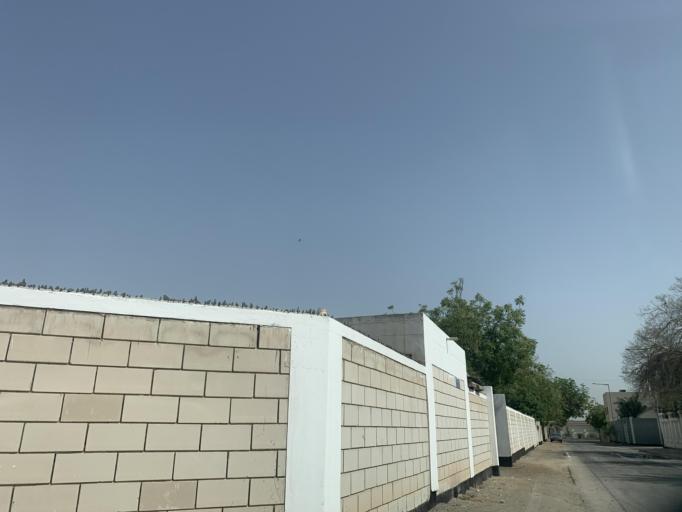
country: BH
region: Northern
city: Madinat `Isa
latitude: 26.1491
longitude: 50.5318
